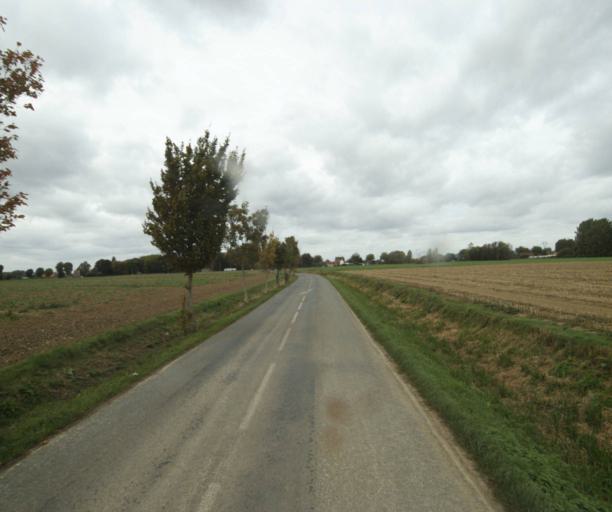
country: FR
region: Nord-Pas-de-Calais
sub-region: Departement du Pas-de-Calais
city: Fleurbaix
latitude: 50.6649
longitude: 2.8161
